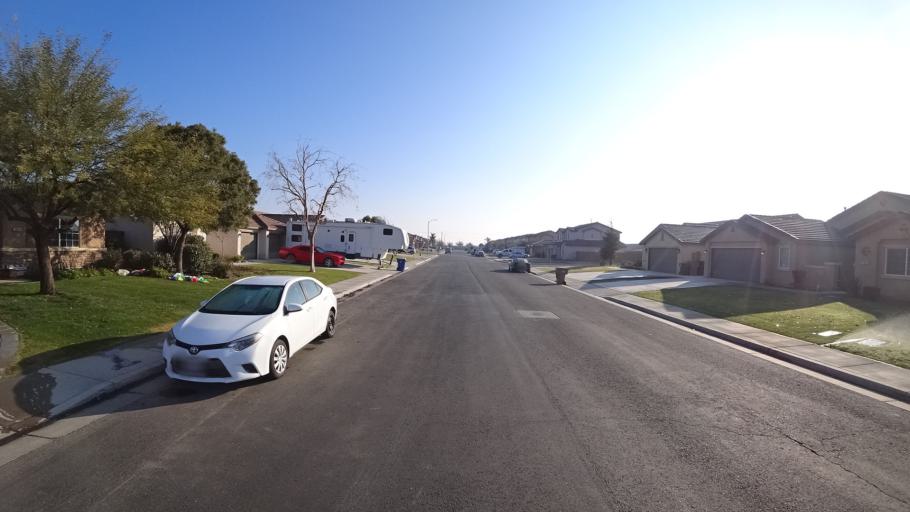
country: US
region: California
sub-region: Kern County
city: Greenacres
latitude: 35.2930
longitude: -119.1221
